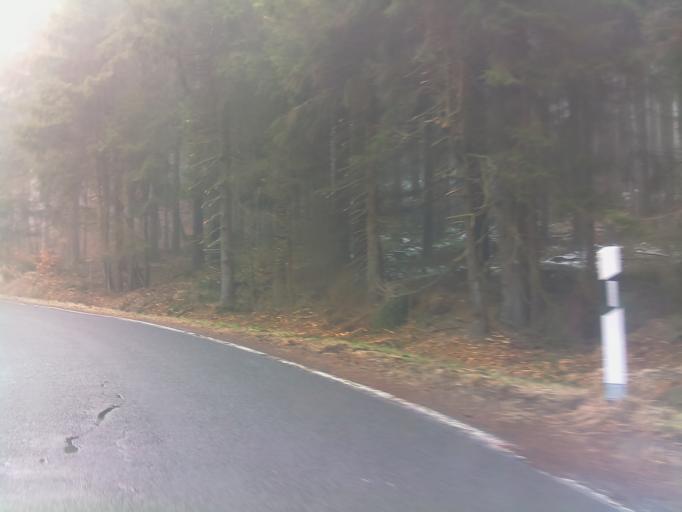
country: DE
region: Rheinland-Pfalz
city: Tiefenbach
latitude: 49.9182
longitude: 7.5769
